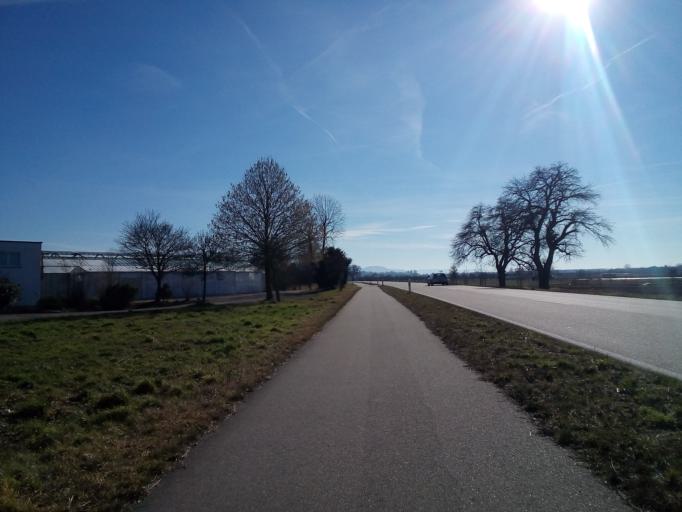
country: DE
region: Baden-Wuerttemberg
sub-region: Freiburg Region
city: Renchen
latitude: 48.6152
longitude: 8.0191
